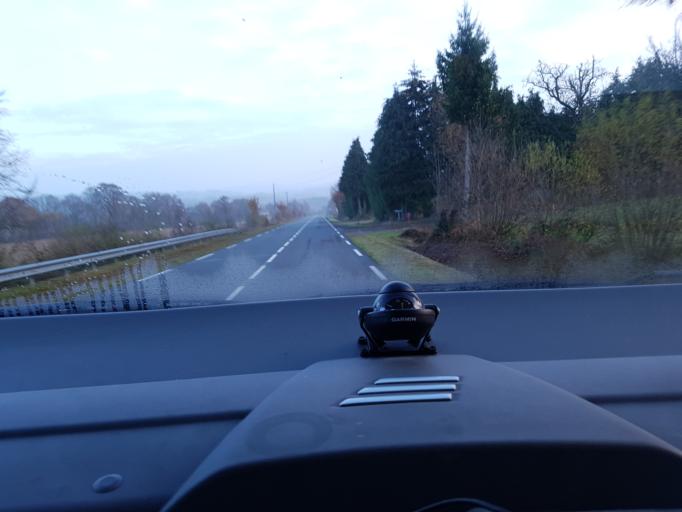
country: FR
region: Lower Normandy
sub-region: Departement de l'Orne
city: Domfront
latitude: 48.5983
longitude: -0.6162
